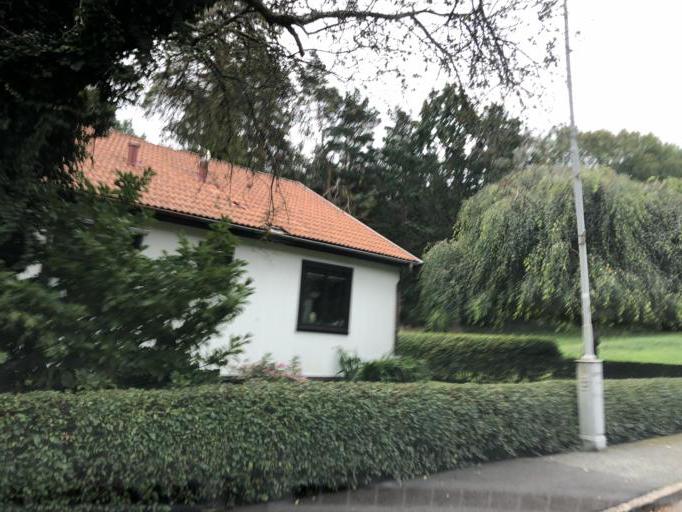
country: SE
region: Vaestra Goetaland
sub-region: Goteborg
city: Majorna
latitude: 57.7347
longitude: 11.9040
